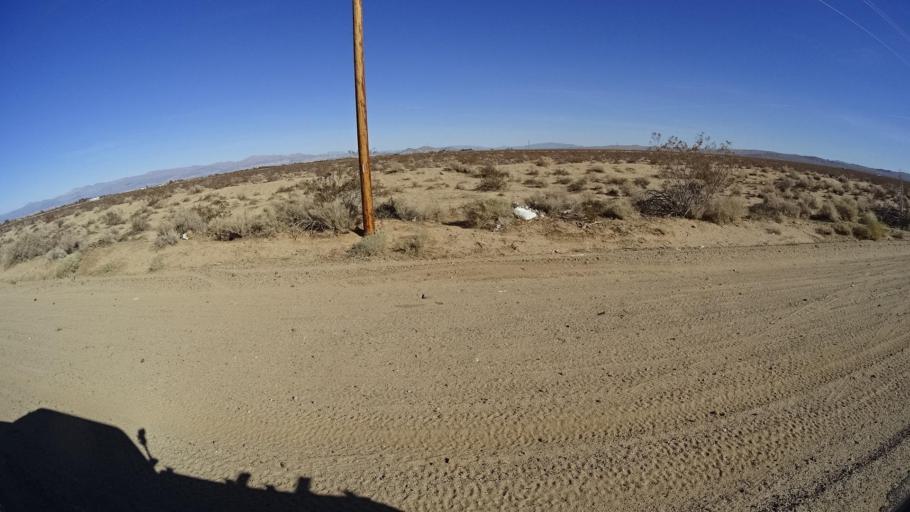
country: US
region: California
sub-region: Kern County
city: Inyokern
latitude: 35.6166
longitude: -117.8033
